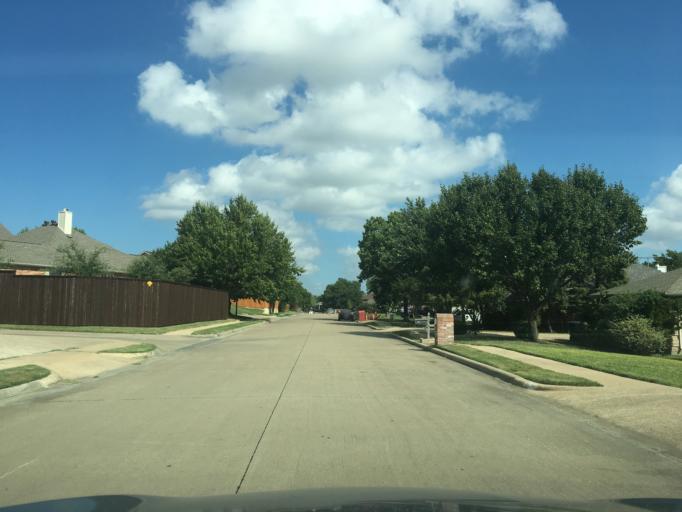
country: US
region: Texas
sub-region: Dallas County
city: Sachse
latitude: 32.9661
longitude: -96.5947
